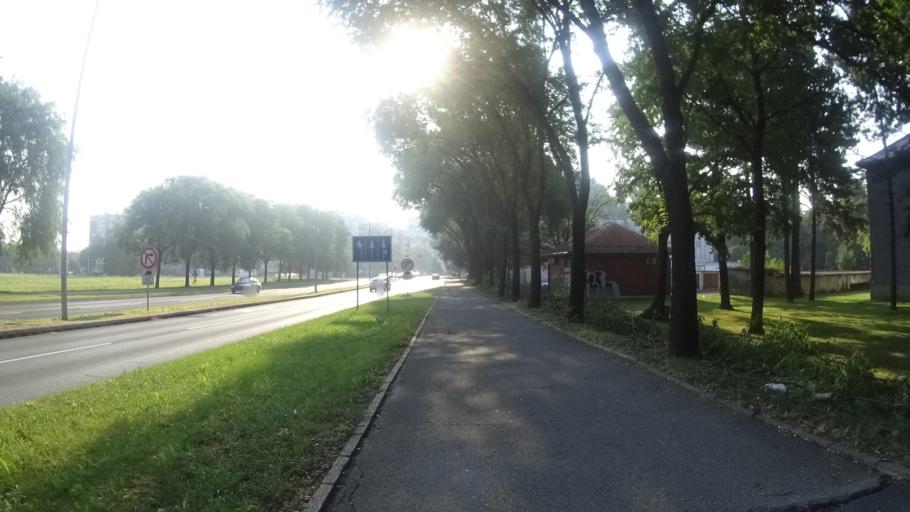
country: HR
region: Varazdinska
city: Varazdin
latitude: 46.3156
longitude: 16.3421
